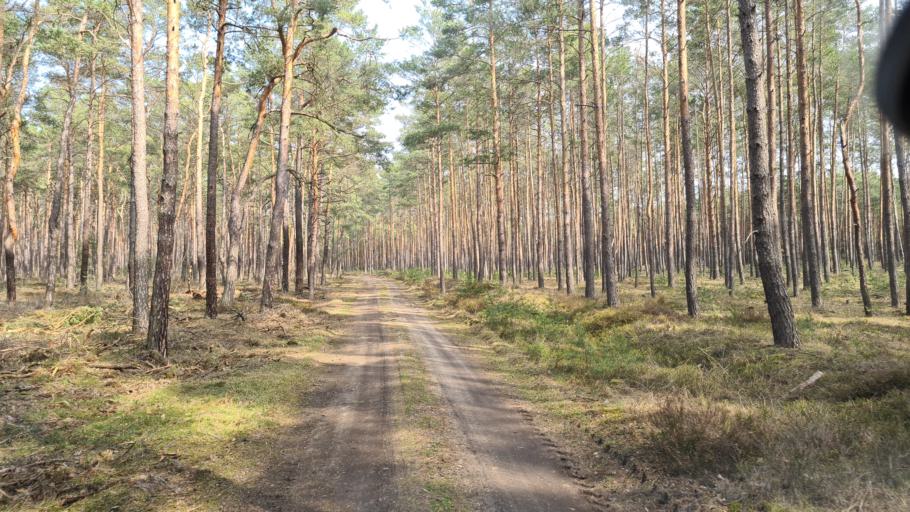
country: DE
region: Brandenburg
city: Trobitz
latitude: 51.6435
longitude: 13.4507
